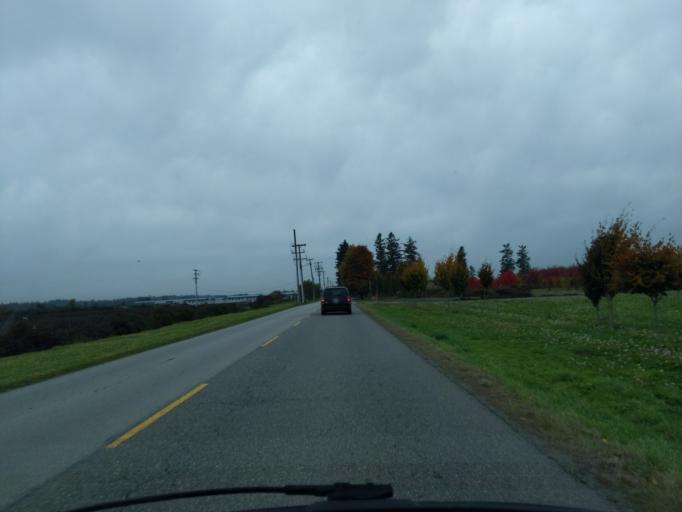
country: CA
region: British Columbia
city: Pitt Meadows
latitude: 49.2225
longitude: -122.7069
